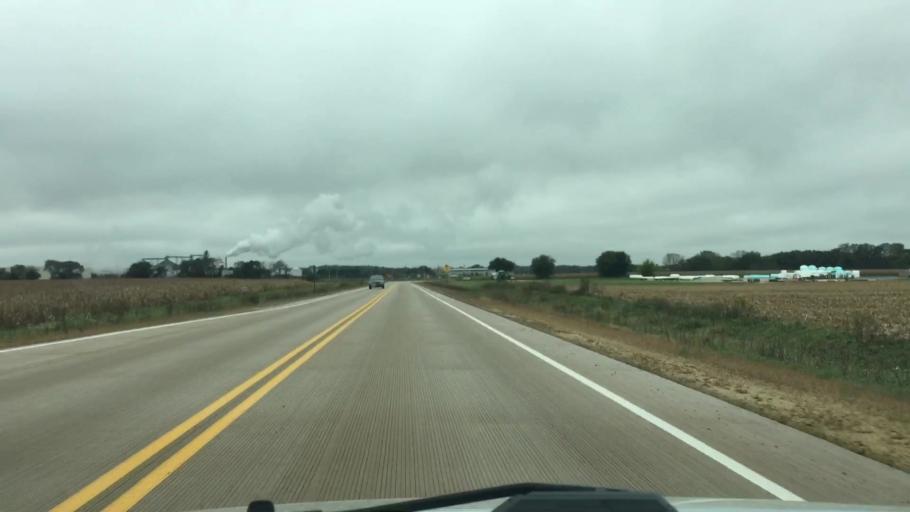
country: US
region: Wisconsin
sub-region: Rock County
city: Milton
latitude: 42.7710
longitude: -88.9064
